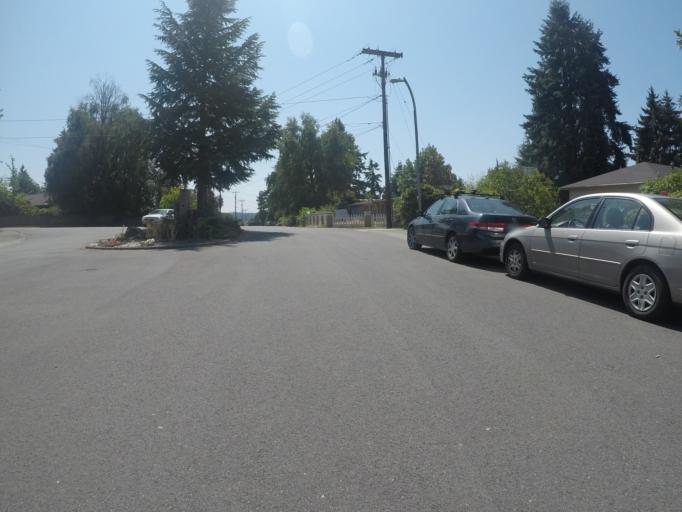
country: US
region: Washington
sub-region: King County
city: Kenmore
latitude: 47.7665
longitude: -122.2602
